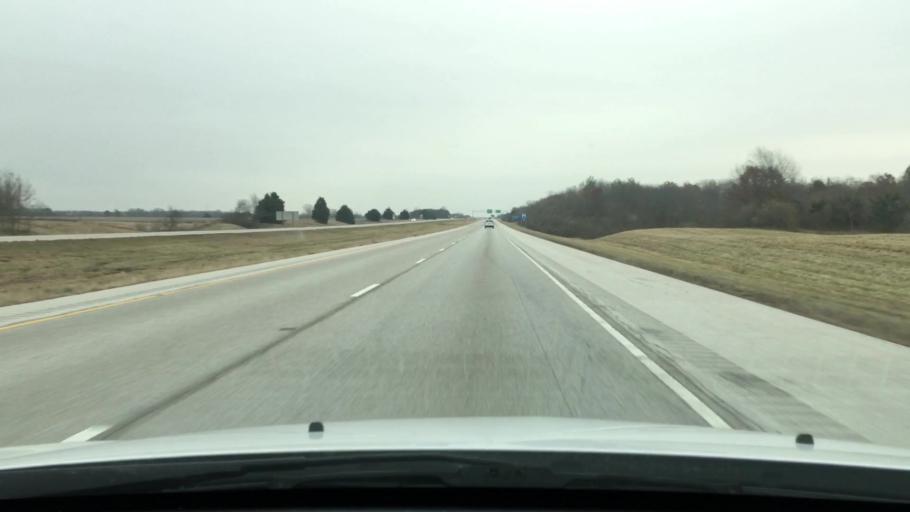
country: US
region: Illinois
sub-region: Morgan County
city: South Jacksonville
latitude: 39.6802
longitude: -90.3112
